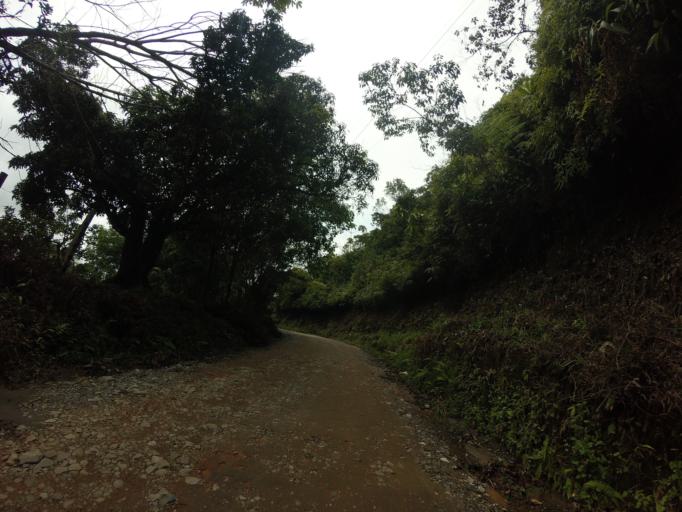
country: CO
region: Caldas
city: Victoria
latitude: 5.3147
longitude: -74.9575
